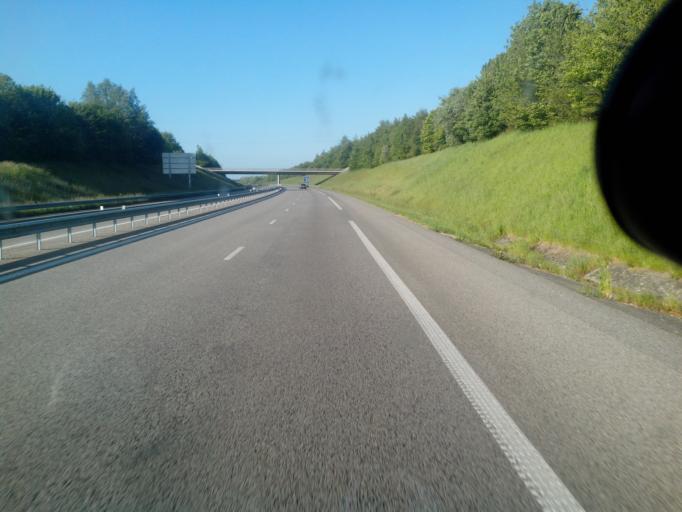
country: FR
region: Haute-Normandie
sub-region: Departement de la Seine-Maritime
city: Saint-Aubin-Routot
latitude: 49.5412
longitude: 0.3269
